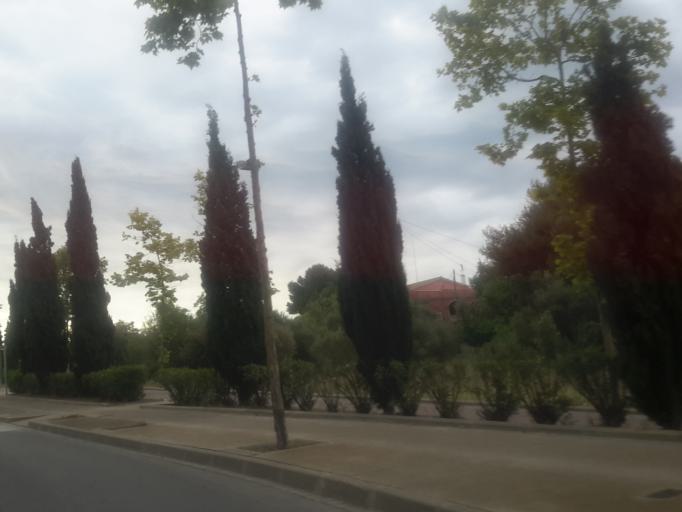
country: ES
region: Catalonia
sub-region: Provincia de Barcelona
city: Vilanova i la Geltru
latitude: 41.2420
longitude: 1.7230
